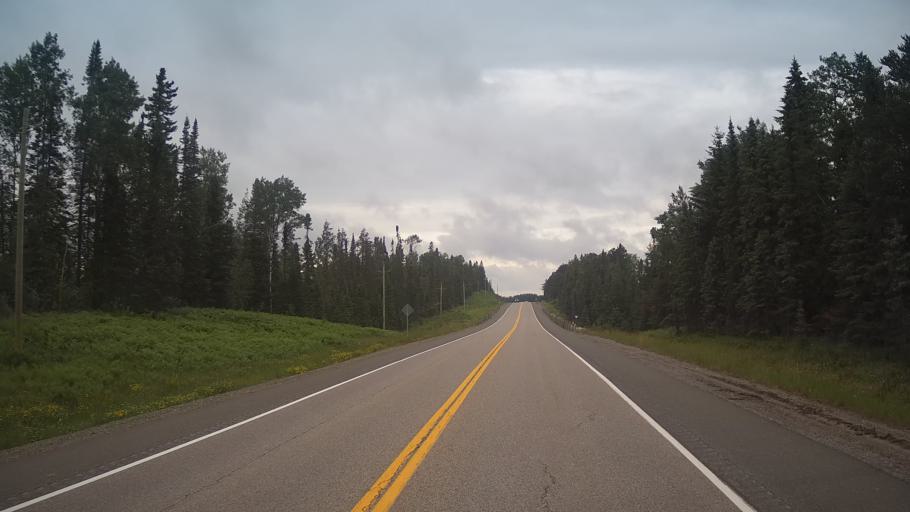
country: CA
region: Ontario
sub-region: Thunder Bay District
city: Thunder Bay
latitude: 48.8346
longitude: -89.9364
